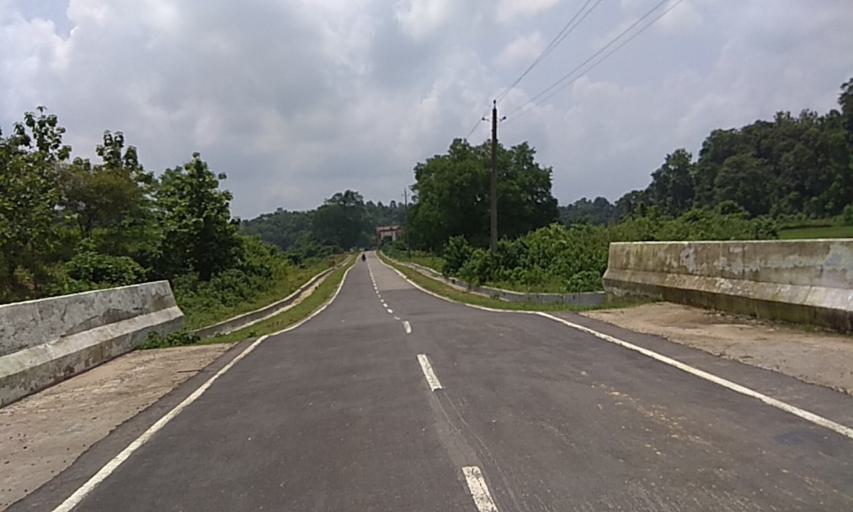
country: BD
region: Chittagong
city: Manikchari
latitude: 22.9364
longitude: 91.9078
